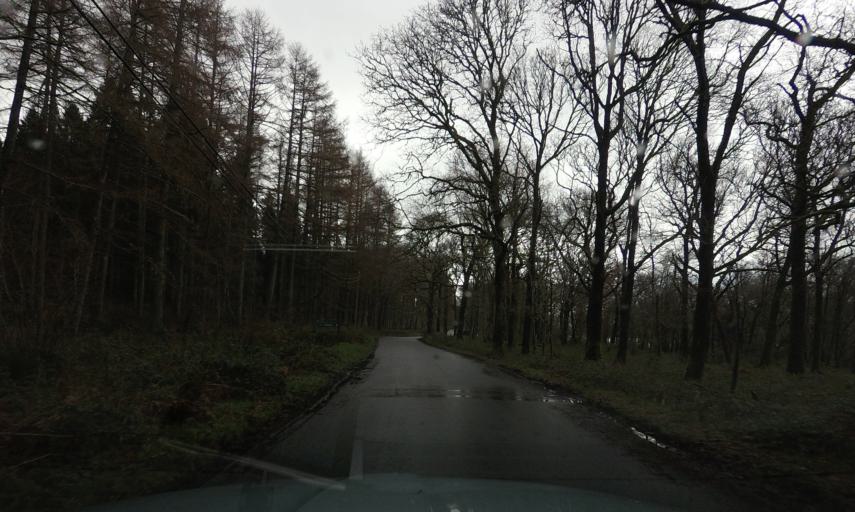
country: GB
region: Scotland
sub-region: West Dunbartonshire
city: Balloch
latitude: 56.1292
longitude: -4.6081
